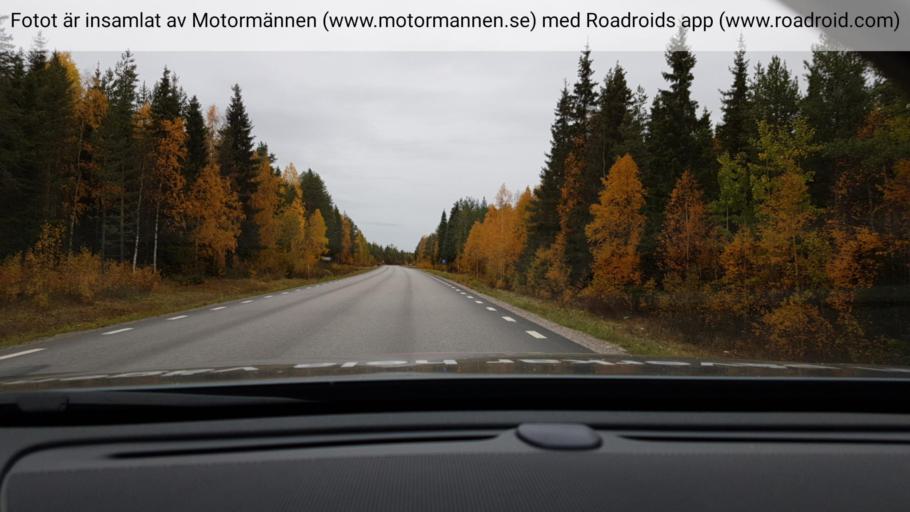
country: SE
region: Norrbotten
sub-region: Overkalix Kommun
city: OEverkalix
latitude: 66.3462
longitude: 22.8290
